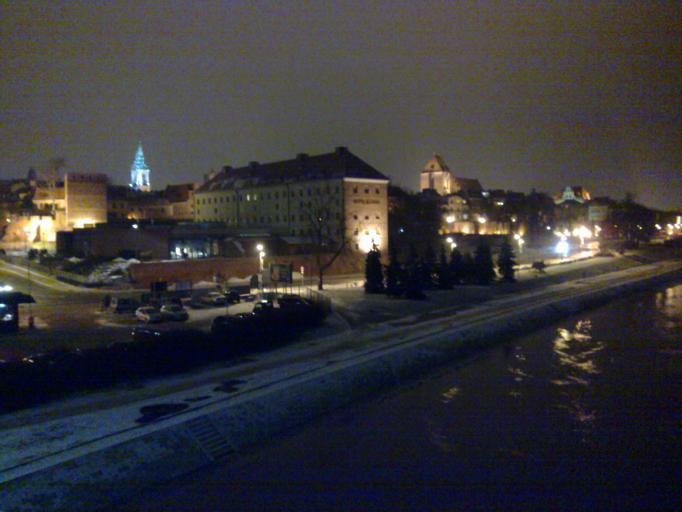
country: PL
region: Kujawsko-Pomorskie
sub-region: Torun
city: Torun
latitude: 53.0068
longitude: 18.6012
